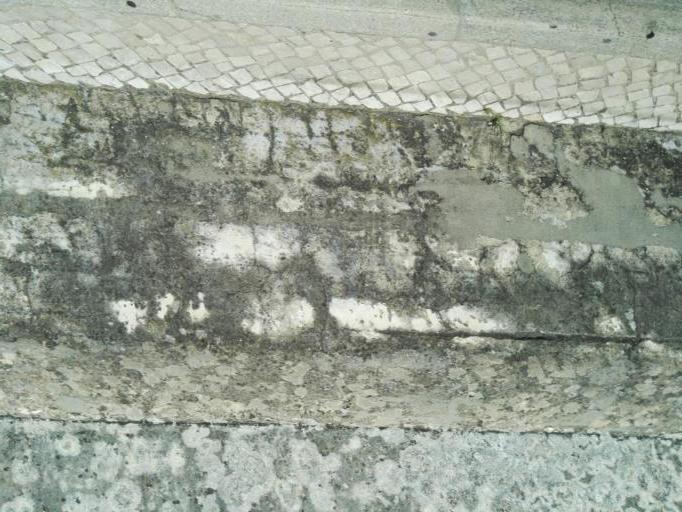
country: PT
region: Santarem
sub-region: Benavente
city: Samora Correia
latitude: 38.9358
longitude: -8.8731
